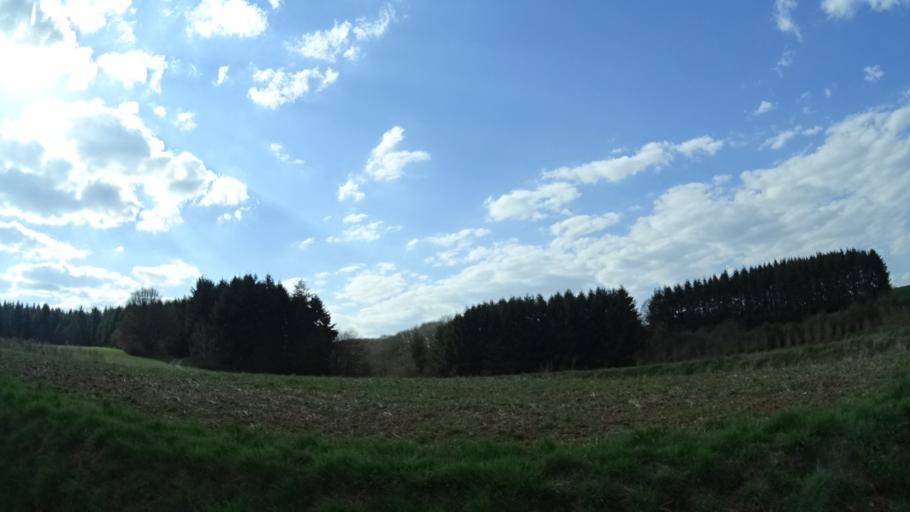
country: DE
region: Rheinland-Pfalz
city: Otzweiler
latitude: 49.7281
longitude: 7.5119
